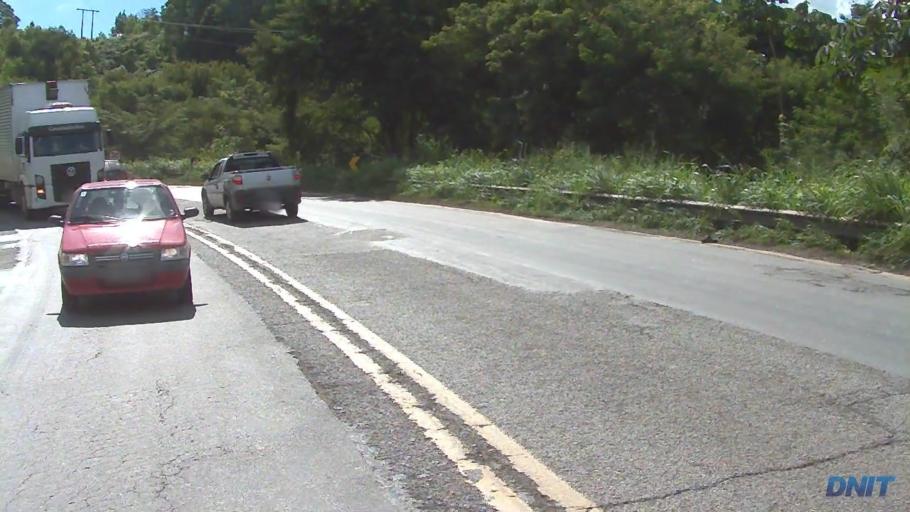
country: BR
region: Minas Gerais
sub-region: Caete
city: Caete
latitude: -19.7451
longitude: -43.5492
